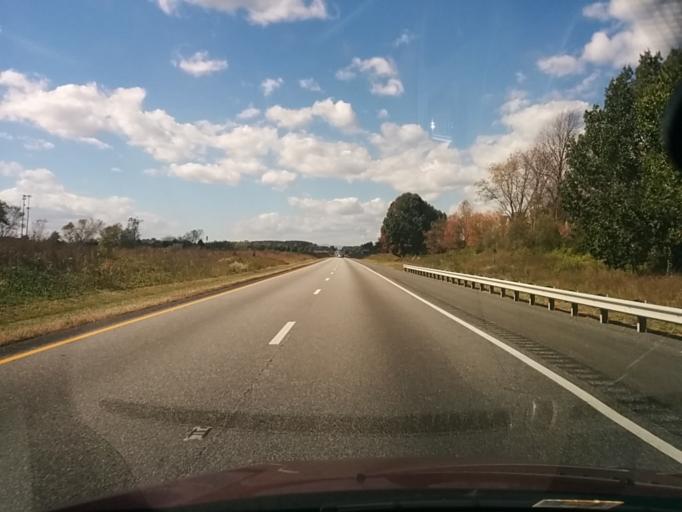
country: US
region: Virginia
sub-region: Augusta County
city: Lyndhurst
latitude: 38.0565
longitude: -78.9254
